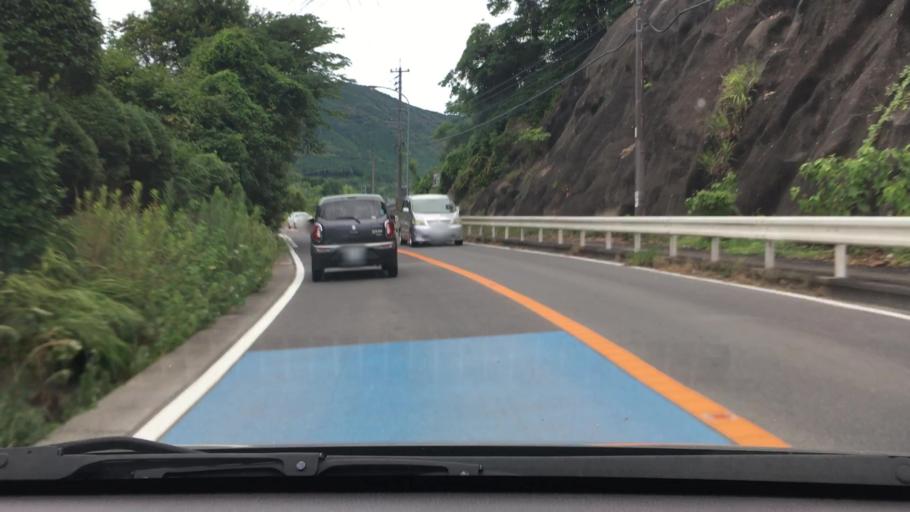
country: JP
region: Nagasaki
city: Sasebo
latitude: 32.9894
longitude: 129.7377
